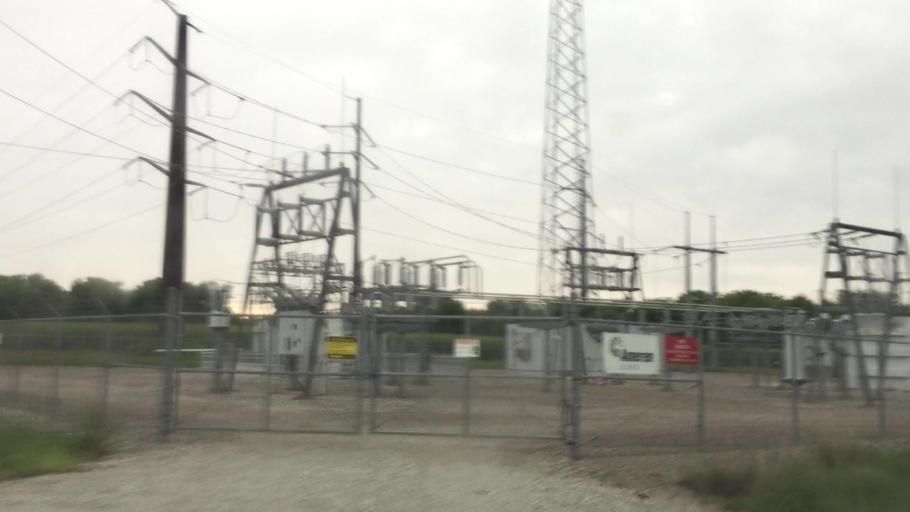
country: US
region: Iowa
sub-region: Lee County
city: Fort Madison
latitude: 40.6071
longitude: -91.2674
